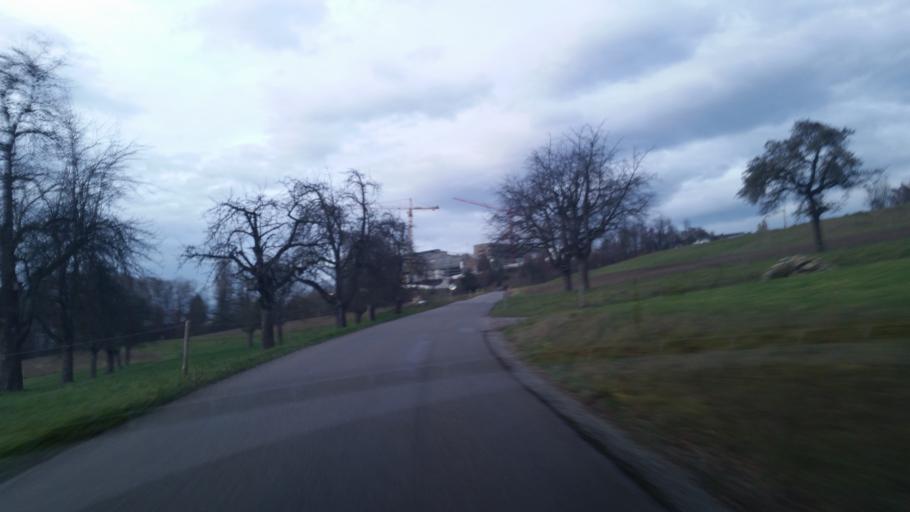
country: CH
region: Aargau
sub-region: Bezirk Baden
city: Kunten
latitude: 47.3824
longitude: 8.3438
